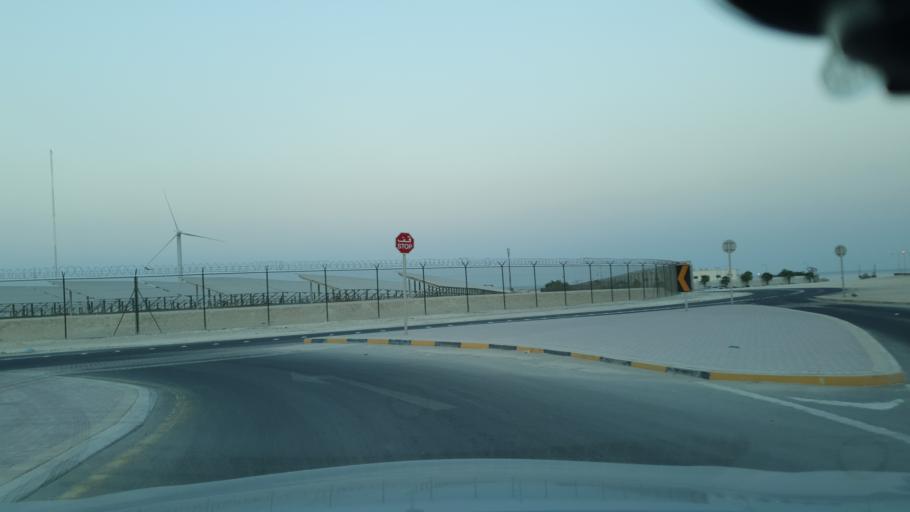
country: BH
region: Central Governorate
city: Dar Kulayb
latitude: 25.9724
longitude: 50.6094
